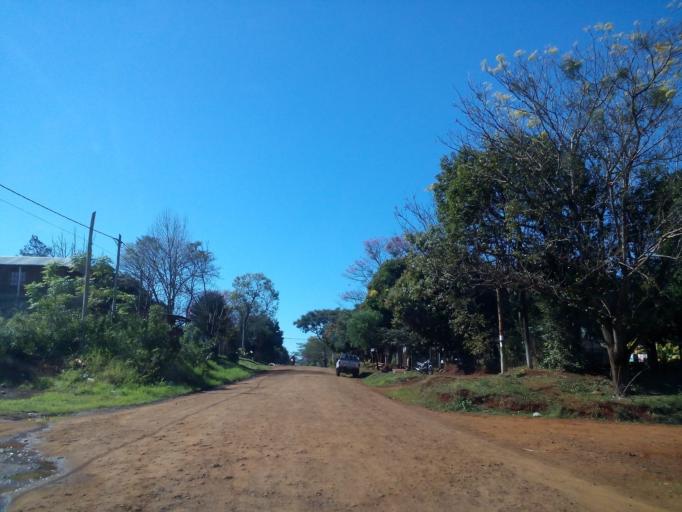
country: AR
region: Misiones
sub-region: Departamento de Capital
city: Posadas
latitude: -27.3903
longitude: -55.9372
